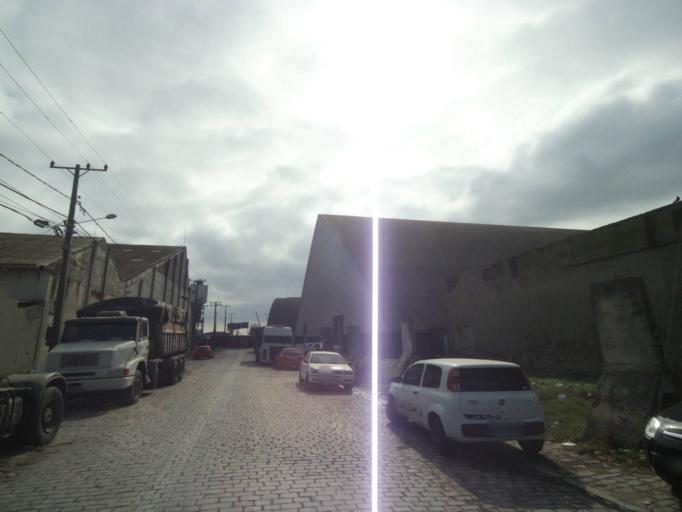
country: BR
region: Parana
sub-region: Paranagua
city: Paranagua
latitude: -25.5101
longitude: -48.5219
